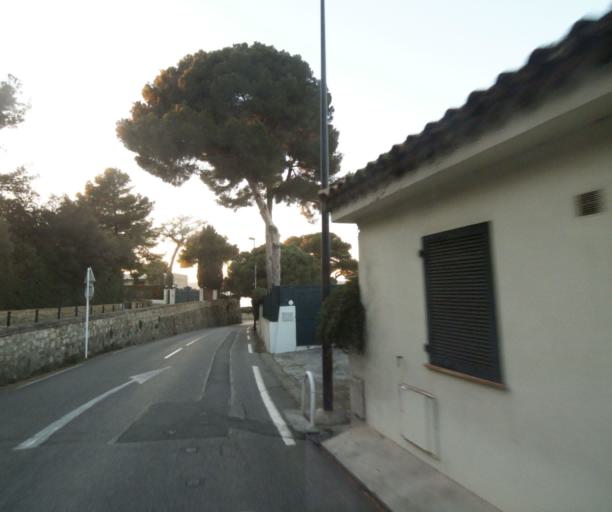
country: FR
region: Provence-Alpes-Cote d'Azur
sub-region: Departement des Alpes-Maritimes
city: Antibes
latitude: 43.5492
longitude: 7.1204
